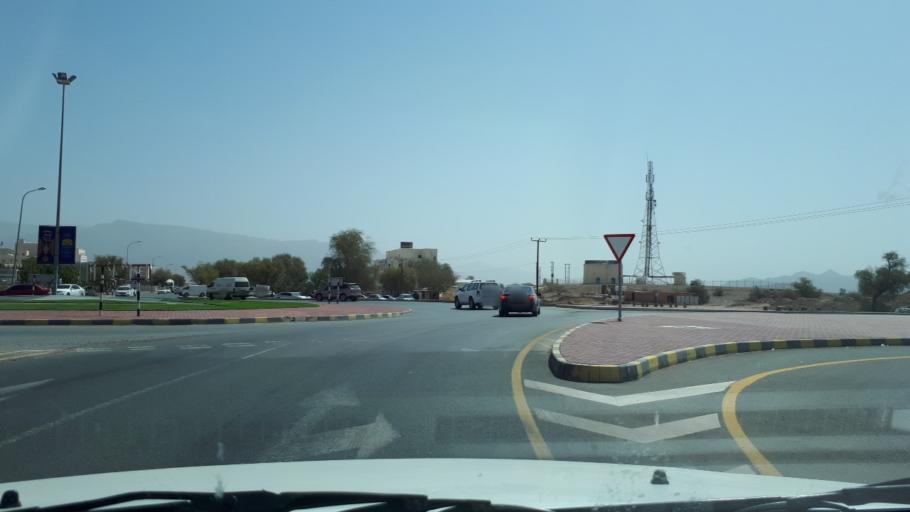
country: OM
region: Muhafazat ad Dakhiliyah
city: Nizwa
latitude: 22.8784
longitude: 57.5365
